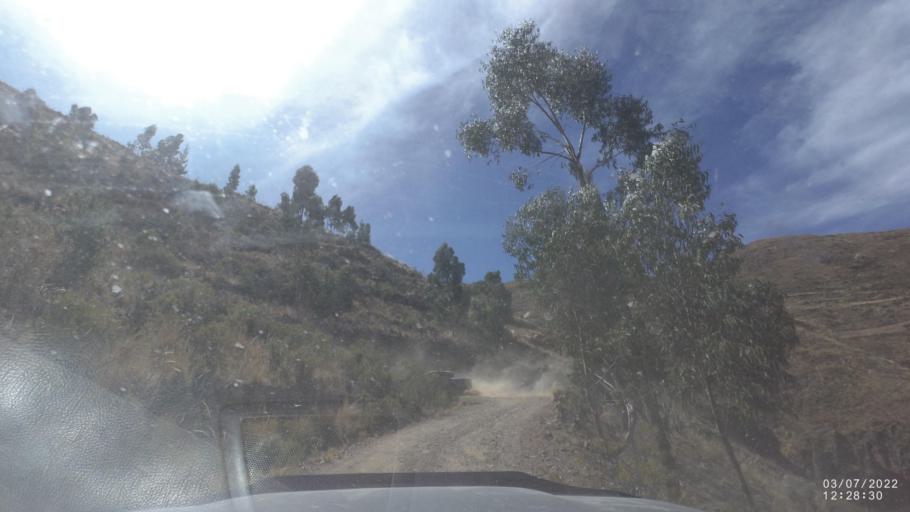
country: BO
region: Cochabamba
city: Irpa Irpa
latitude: -17.8115
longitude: -66.6109
